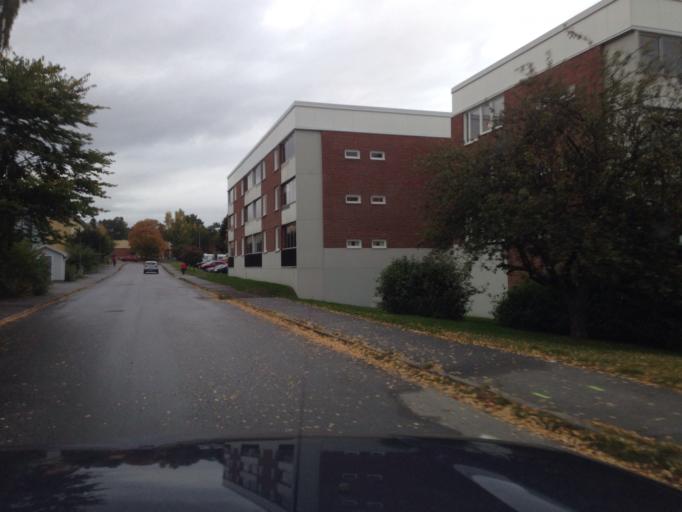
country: SE
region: Vaesternorrland
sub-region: Sundsvalls Kommun
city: Sundsvall
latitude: 62.3994
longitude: 17.3307
